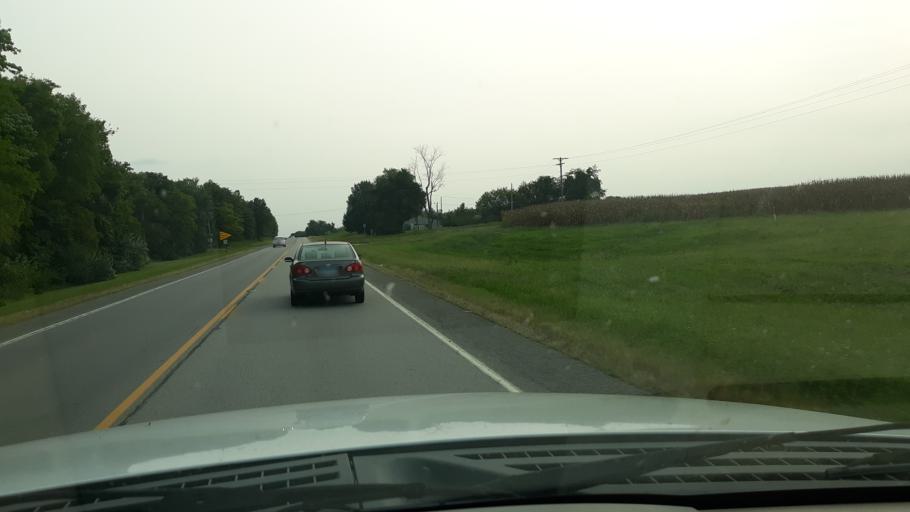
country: US
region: Illinois
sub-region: Edwards County
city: Grayville
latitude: 38.1876
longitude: -88.0398
